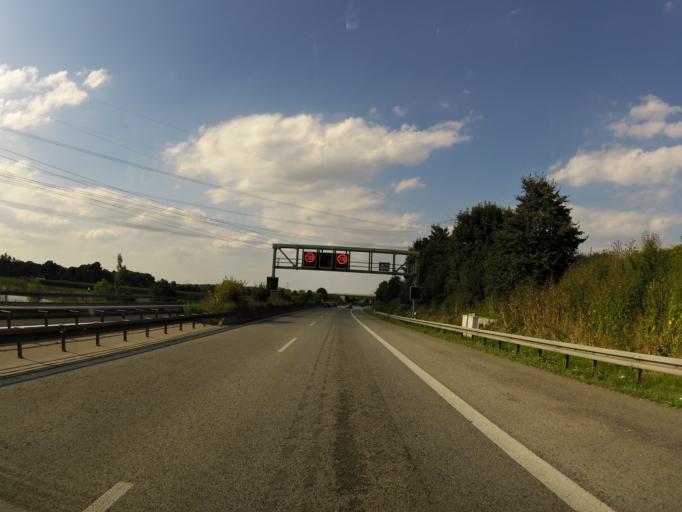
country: DE
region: Bavaria
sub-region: Upper Bavaria
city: Karlsfeld
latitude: 48.1954
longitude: 11.4371
